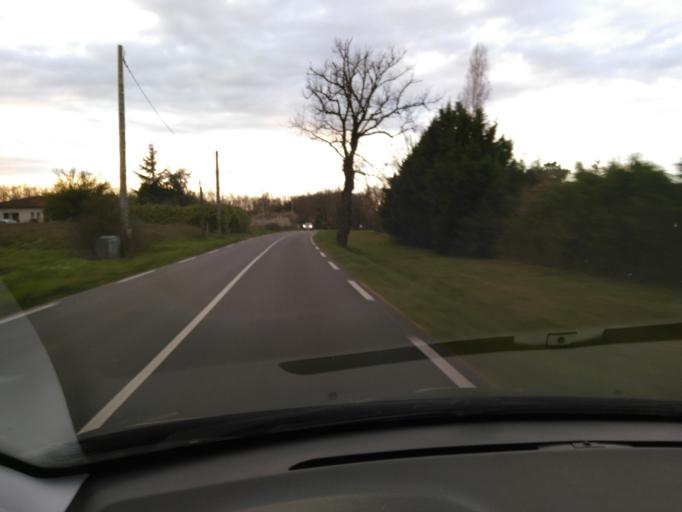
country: FR
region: Midi-Pyrenees
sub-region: Departement de la Haute-Garonne
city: Brax
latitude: 43.6129
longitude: 1.2616
